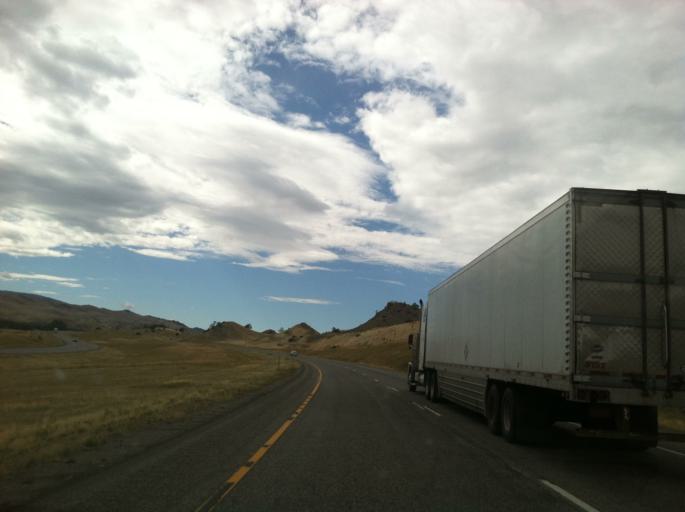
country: US
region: Montana
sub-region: Park County
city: Livingston
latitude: 45.6621
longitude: -110.6430
